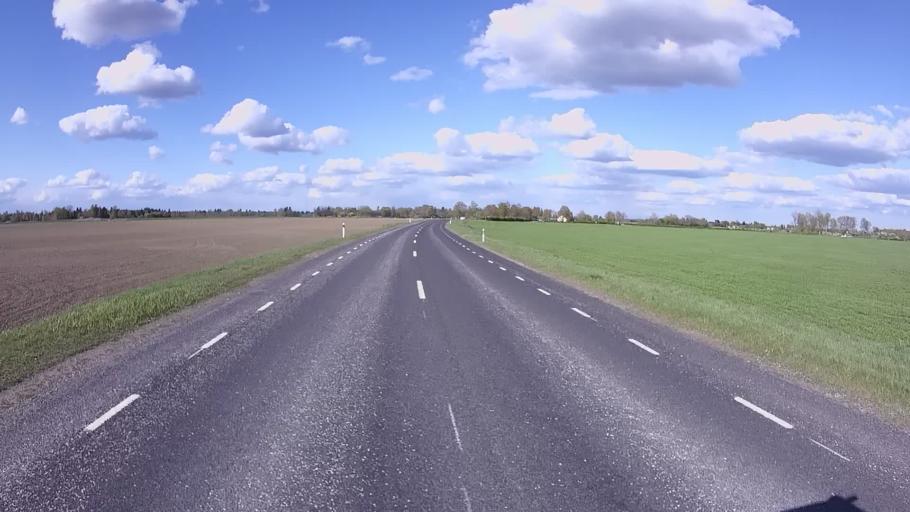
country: EE
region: Jogevamaa
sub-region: Jogeva linn
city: Jogeva
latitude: 58.7232
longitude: 26.1900
